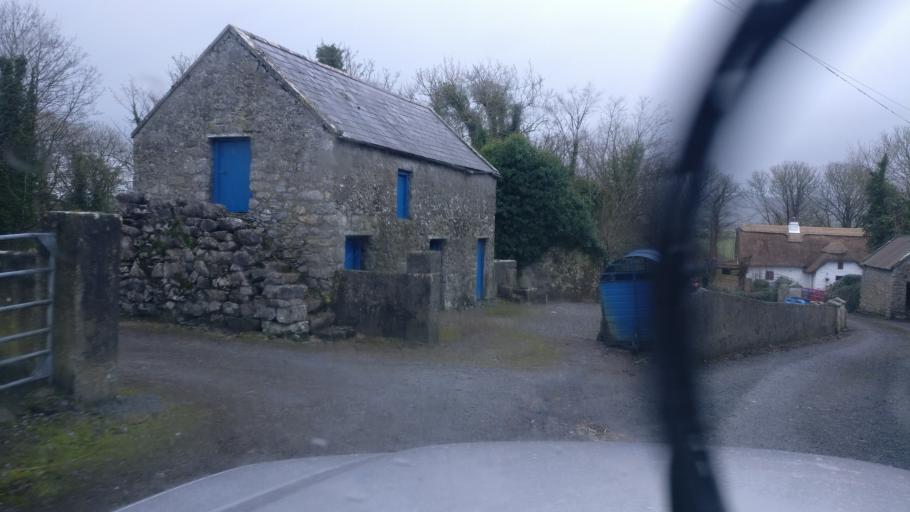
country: IE
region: Connaught
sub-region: County Galway
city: Loughrea
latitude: 53.1905
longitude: -8.6789
